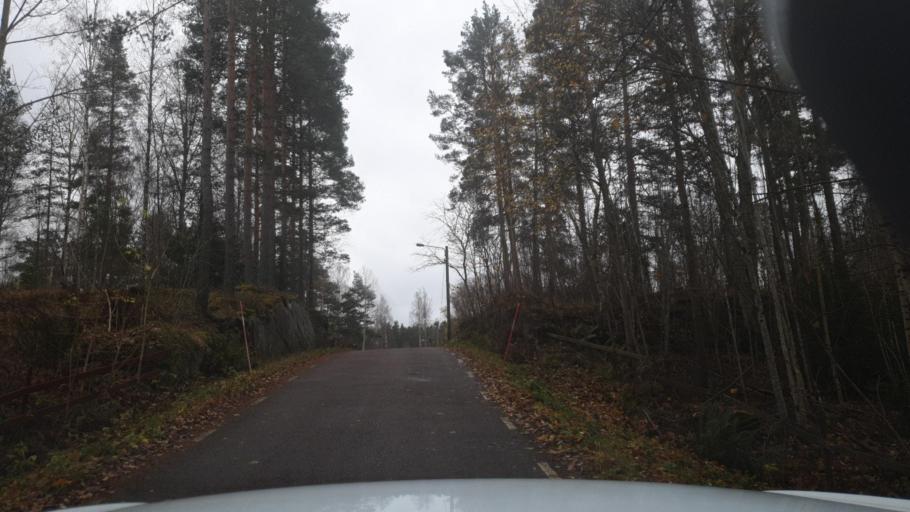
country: SE
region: Vaermland
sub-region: Arvika Kommun
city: Arvika
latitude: 59.5328
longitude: 12.4792
